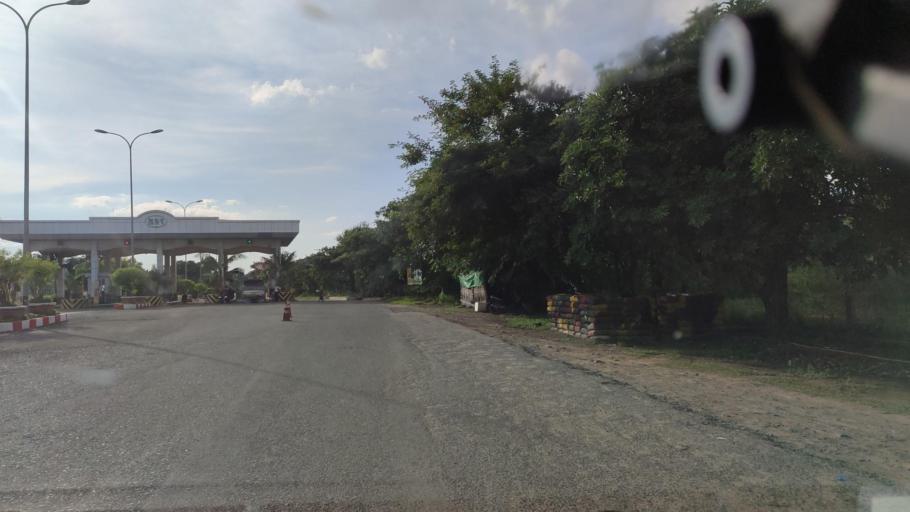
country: MM
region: Magway
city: Chauk
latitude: 20.8157
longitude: 95.1907
